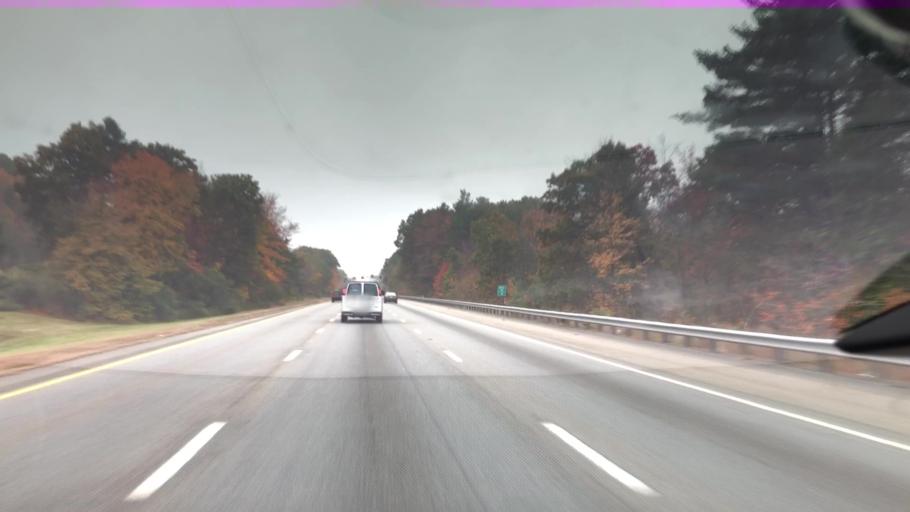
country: US
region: Massachusetts
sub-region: Worcester County
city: Harvard
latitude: 42.4653
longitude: -71.5647
